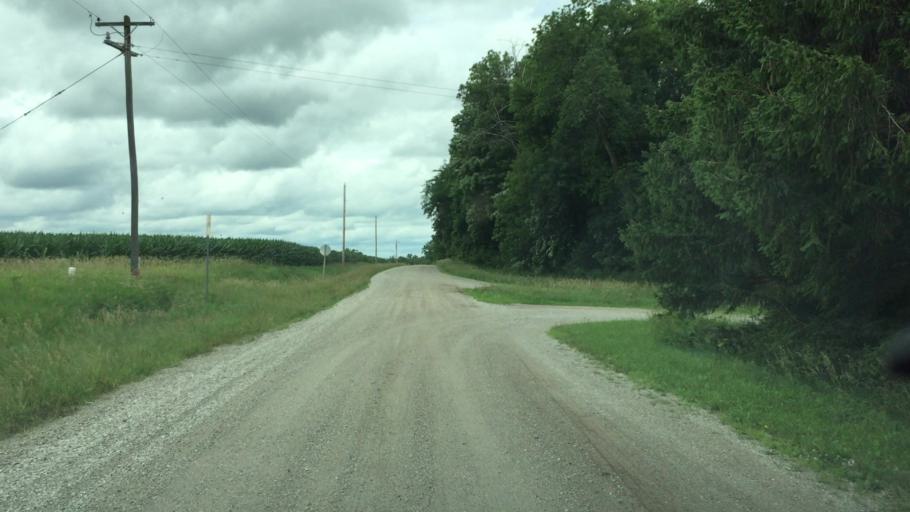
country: US
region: Iowa
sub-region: Jasper County
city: Monroe
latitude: 41.5950
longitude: -93.1161
